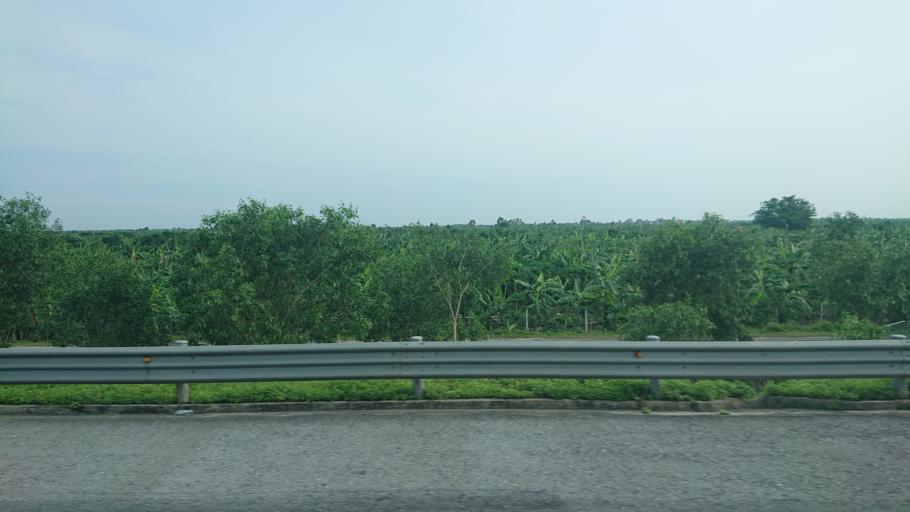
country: VN
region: Hai Duong
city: Tu Ky
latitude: 20.8217
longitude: 106.4740
